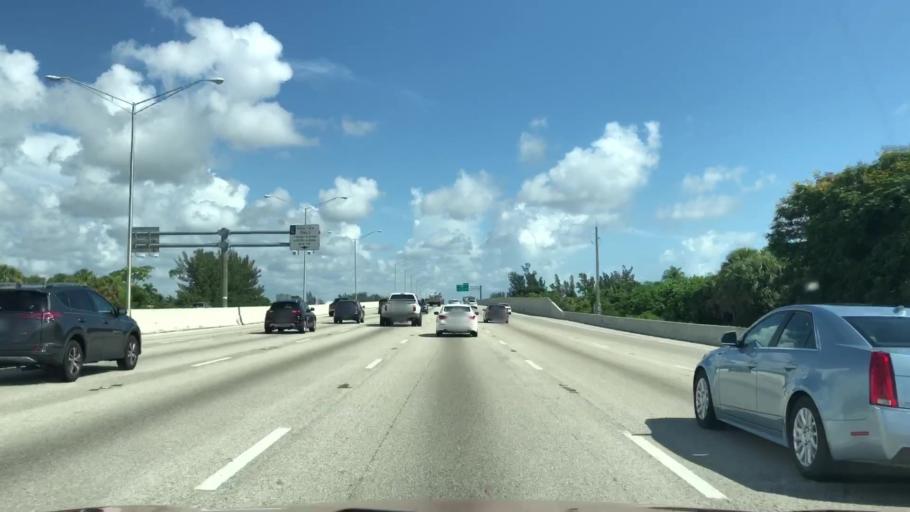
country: US
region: Florida
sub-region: Palm Beach County
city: Lake Clarke Shores
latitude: 26.6317
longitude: -80.0685
